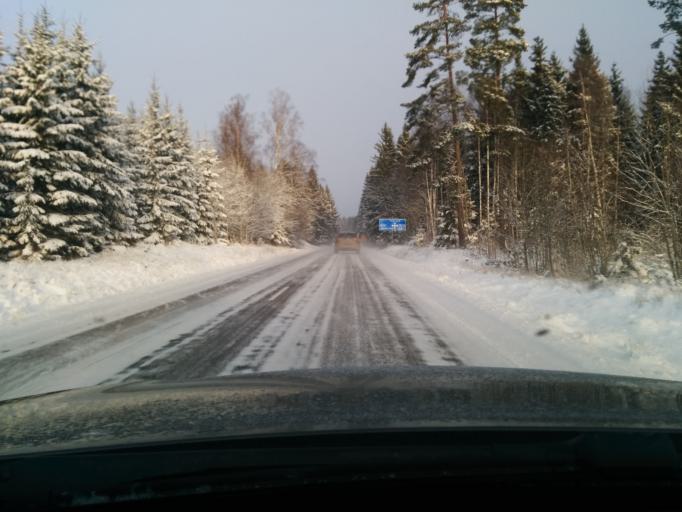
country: SE
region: Uppsala
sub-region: Tierps Kommun
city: Orbyhus
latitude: 60.2134
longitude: 17.7006
